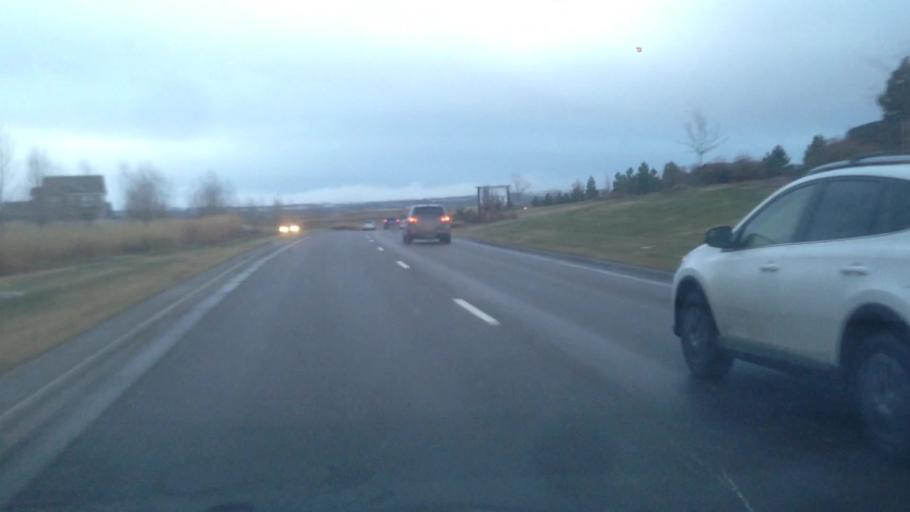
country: US
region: Colorado
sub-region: Douglas County
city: Stonegate
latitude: 39.5199
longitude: -104.8274
